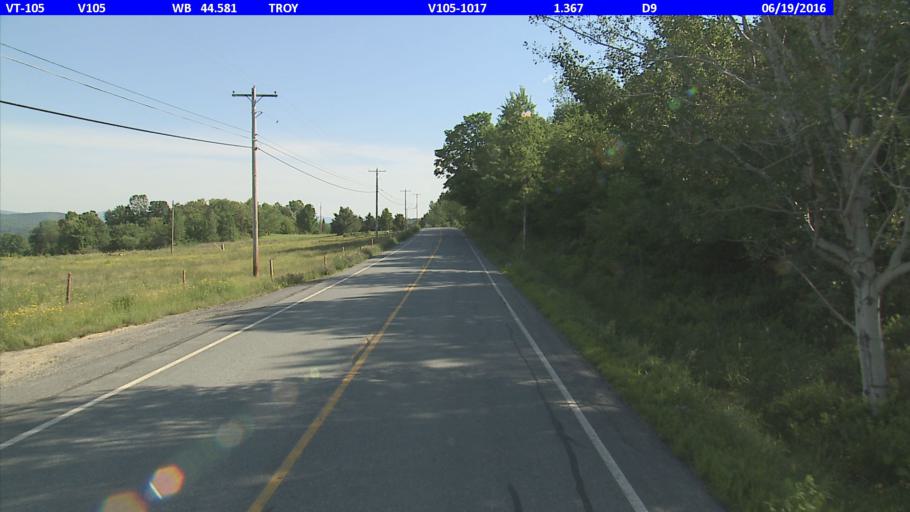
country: US
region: Vermont
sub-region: Orleans County
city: Newport
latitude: 44.9784
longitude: -72.4131
